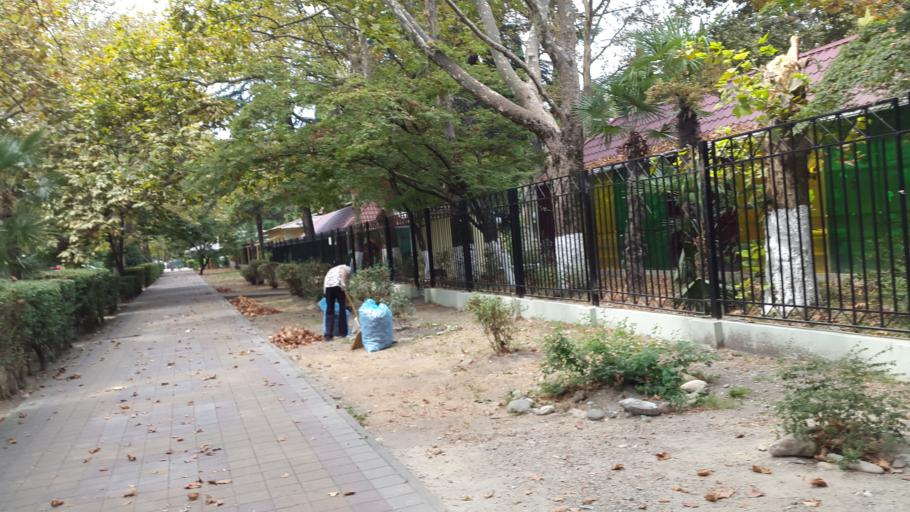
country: RU
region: Krasnodarskiy
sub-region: Sochi City
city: Sochi
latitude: 43.6012
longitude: 39.7270
